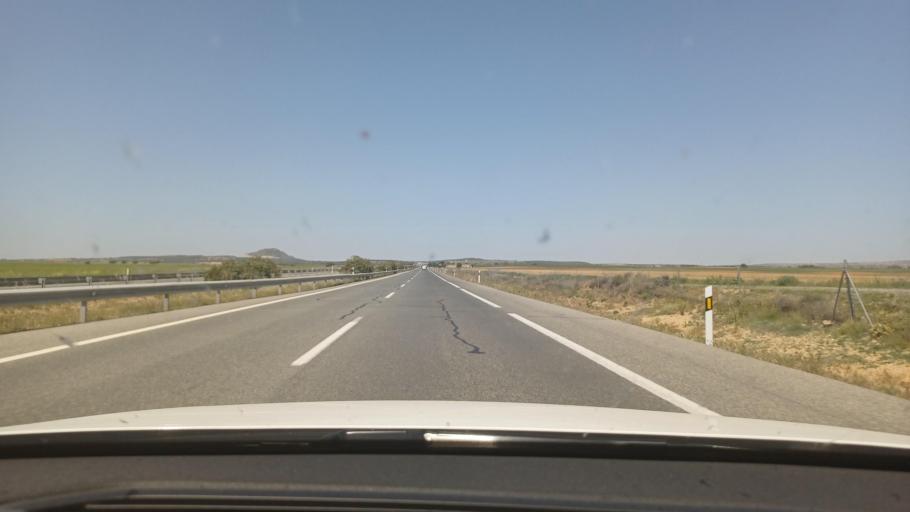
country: ES
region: Castille-La Mancha
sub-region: Provincia de Albacete
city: Bonete
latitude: 38.8825
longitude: -1.3854
